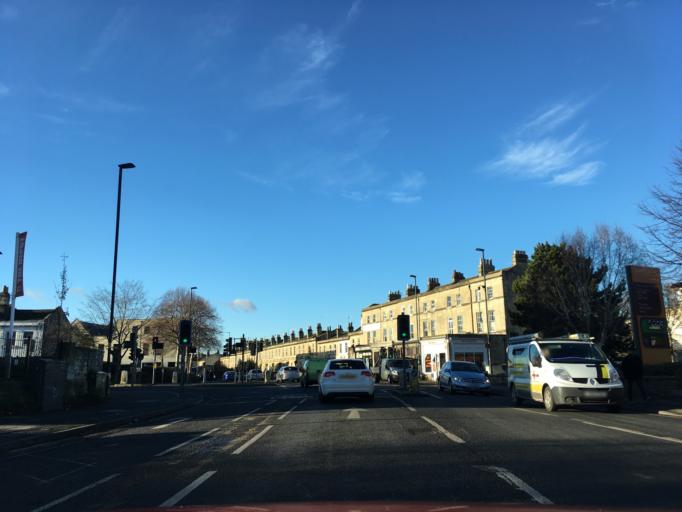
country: GB
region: England
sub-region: Bath and North East Somerset
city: Bath
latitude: 51.3809
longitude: -2.3736
